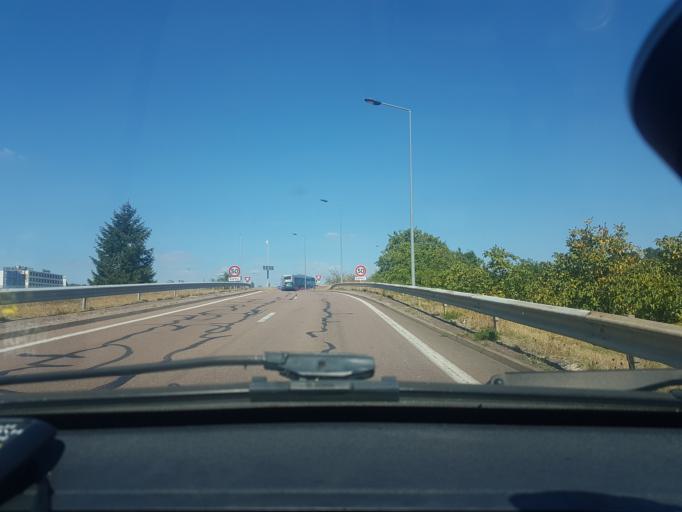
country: FR
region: Bourgogne
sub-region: Departement de la Cote-d'Or
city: Saint-Apollinaire
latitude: 47.3247
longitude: 5.0789
